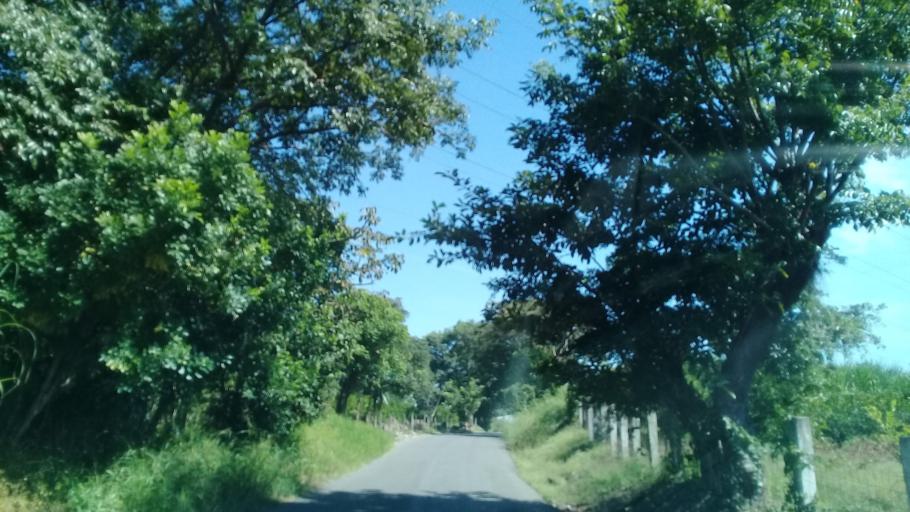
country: MX
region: Veracruz
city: Amatlan de los Reyes
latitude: 18.8577
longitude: -96.9056
